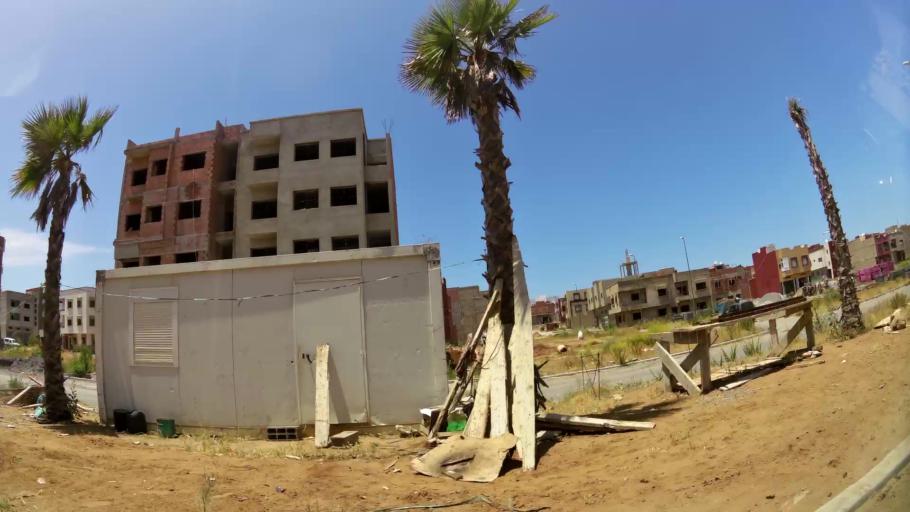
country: MA
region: Gharb-Chrarda-Beni Hssen
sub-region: Kenitra Province
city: Kenitra
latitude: 34.2460
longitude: -6.6514
